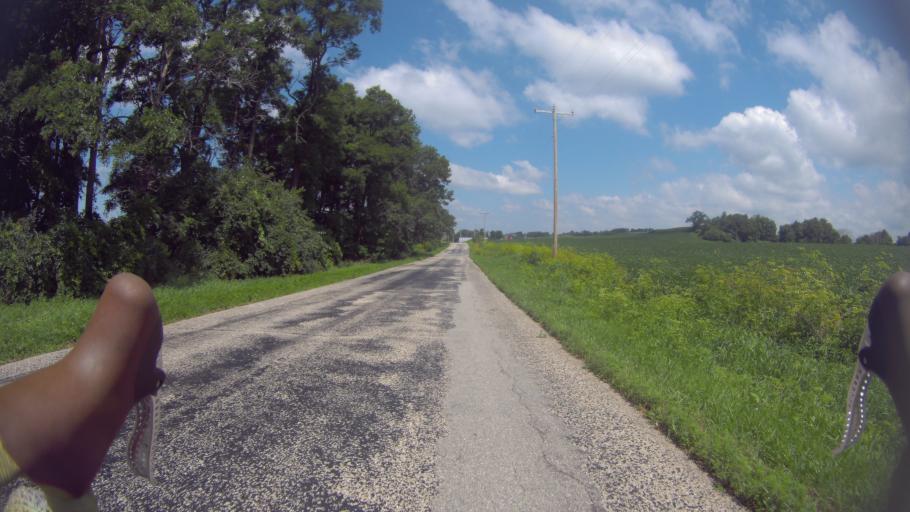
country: US
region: Wisconsin
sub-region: Columbia County
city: Lodi
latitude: 43.2353
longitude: -89.5994
